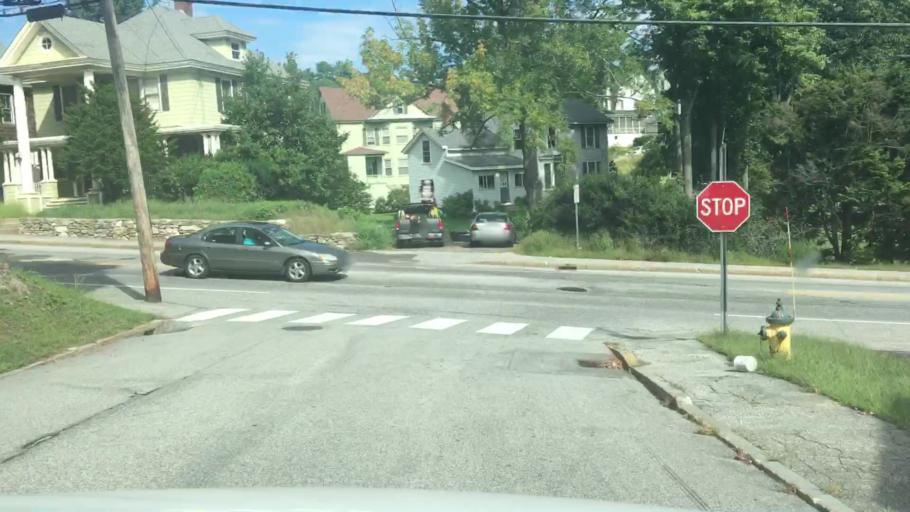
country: US
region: Maine
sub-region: Androscoggin County
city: Auburn
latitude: 44.0976
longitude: -70.2360
